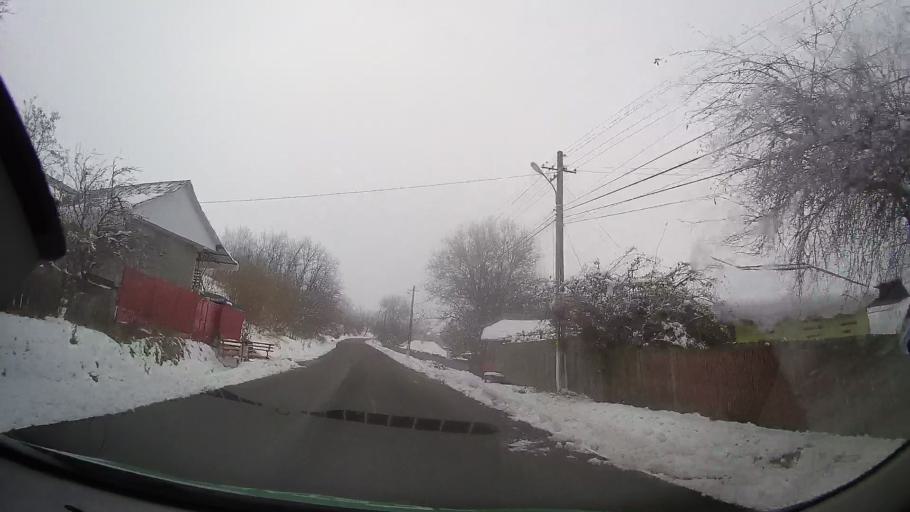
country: RO
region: Bacau
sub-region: Comuna Oncesti
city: Oncesti
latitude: 46.4711
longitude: 27.2561
